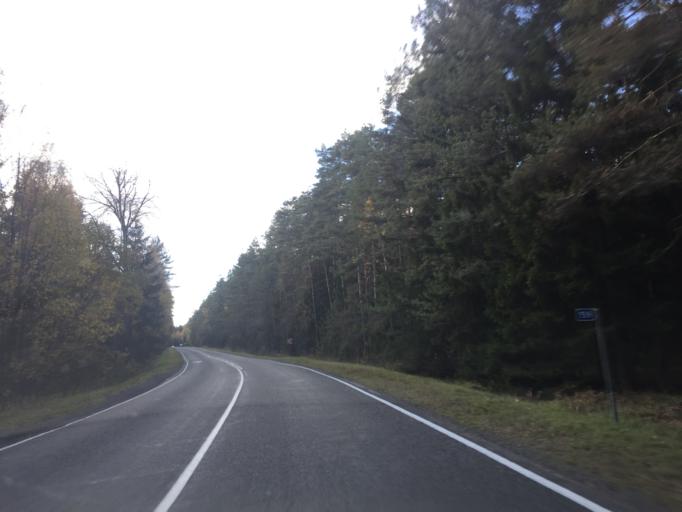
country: BY
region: Minsk
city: Narach
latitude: 54.9537
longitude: 26.6022
